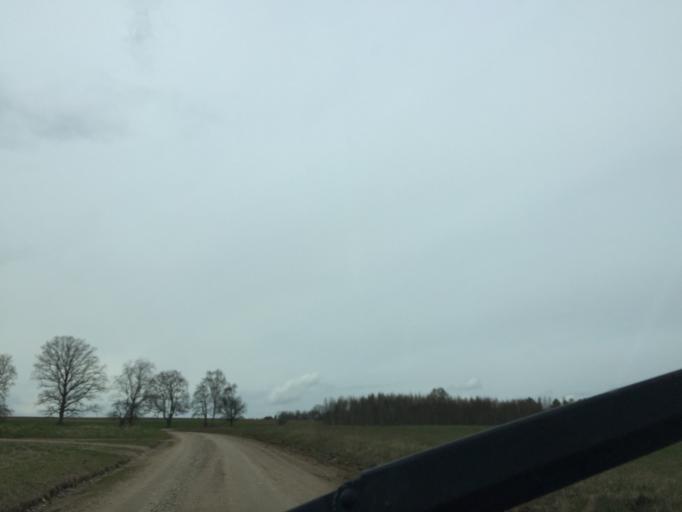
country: LV
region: Priekuli
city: Priekuli
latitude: 57.3342
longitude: 25.3794
